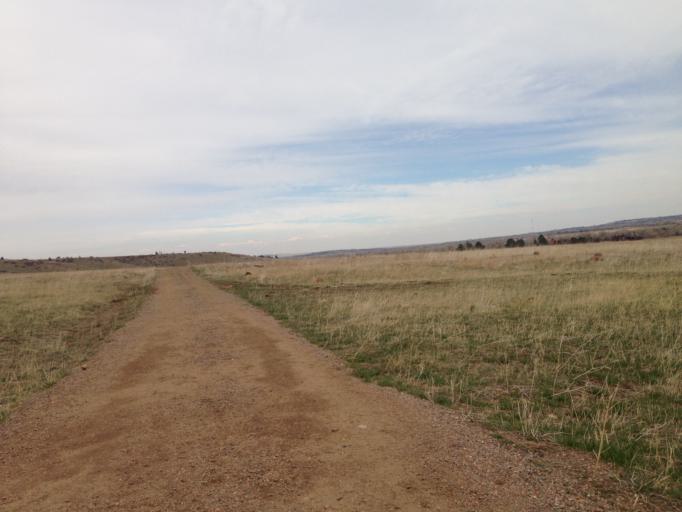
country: US
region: Colorado
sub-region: Boulder County
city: Boulder
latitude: 39.9572
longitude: -105.2506
